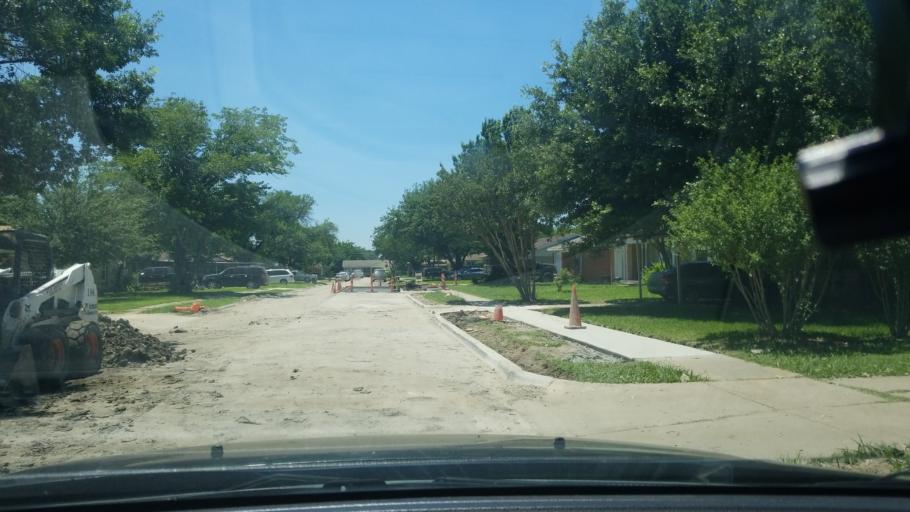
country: US
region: Texas
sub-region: Dallas County
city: Mesquite
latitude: 32.7789
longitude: -96.6099
